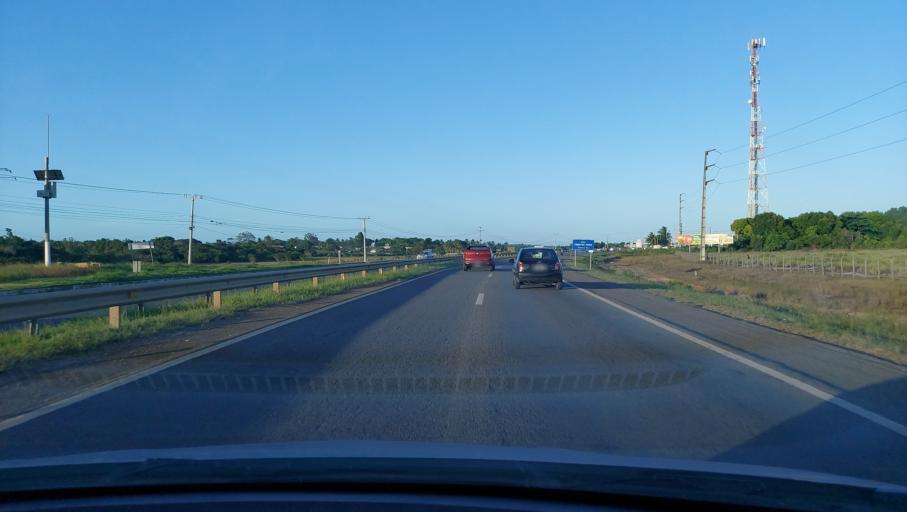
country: BR
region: Bahia
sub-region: Camacari
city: Camacari
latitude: -12.7237
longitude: -38.1596
